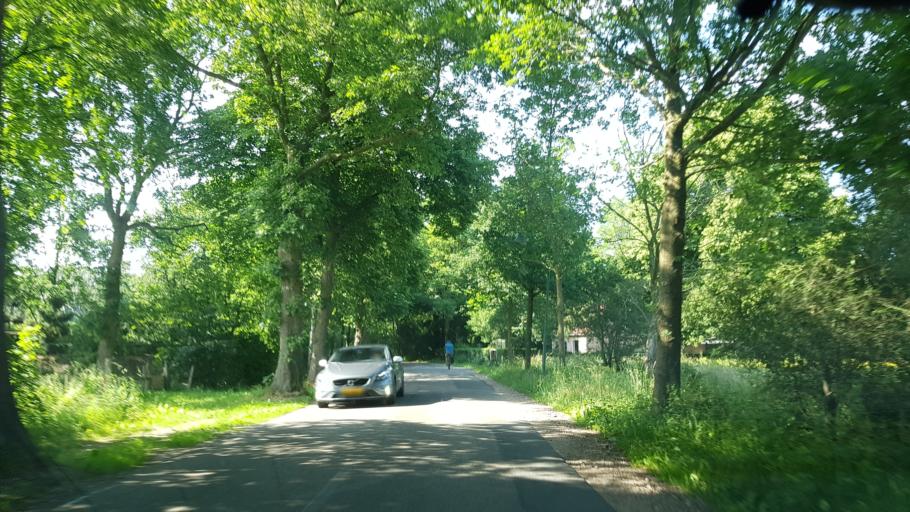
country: NL
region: North Brabant
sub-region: Gemeente Breda
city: Hoge Vucht
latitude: 51.6288
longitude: 4.8214
